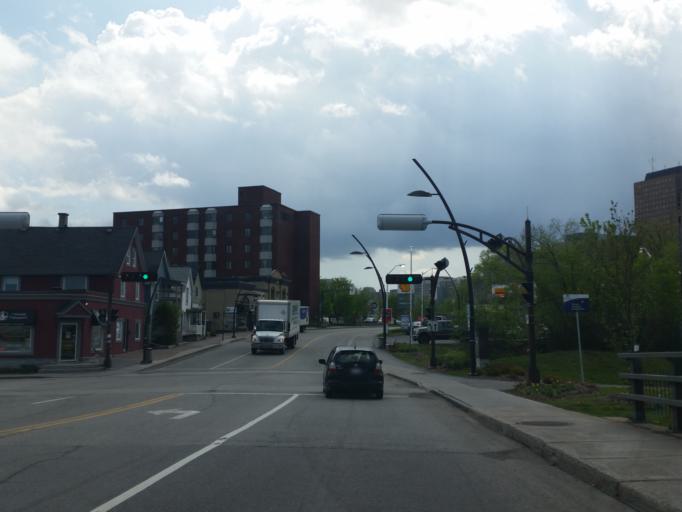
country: CA
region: Ontario
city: Ottawa
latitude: 45.4295
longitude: -75.7271
